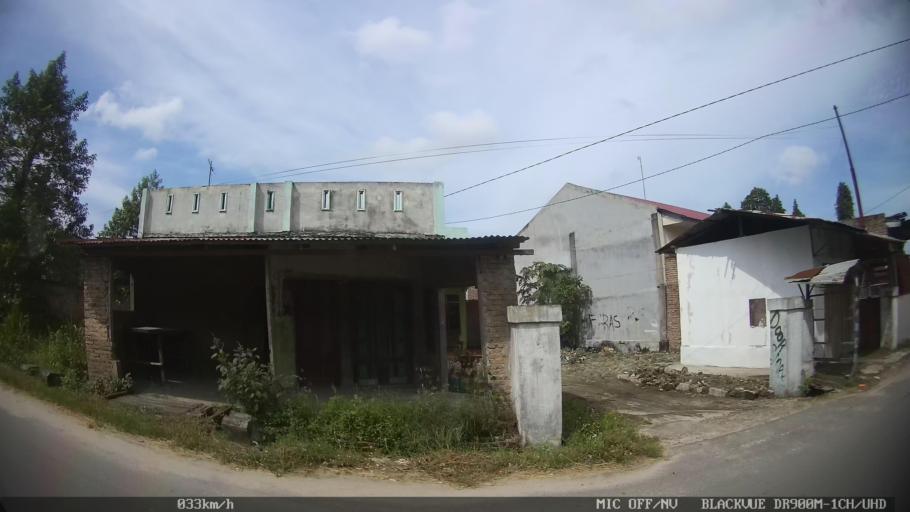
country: ID
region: North Sumatra
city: Percut
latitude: 3.6063
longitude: 98.8546
